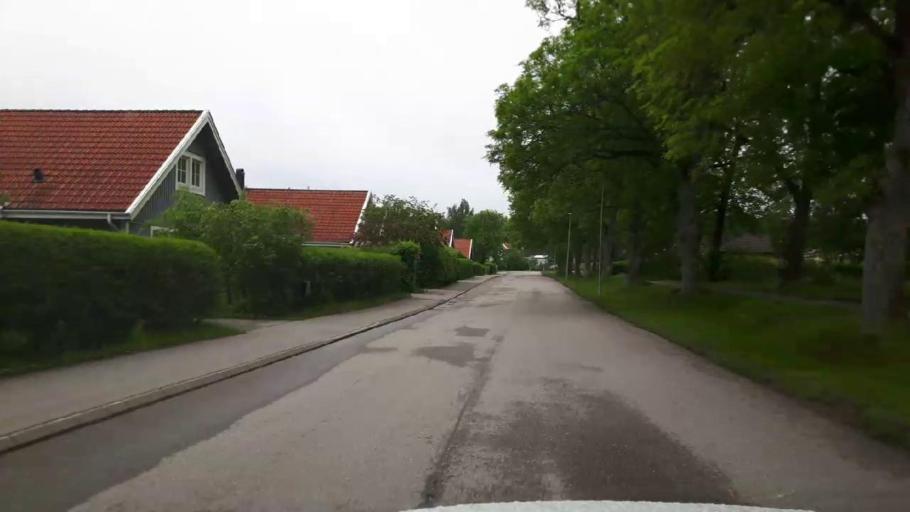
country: SE
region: Stockholm
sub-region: Upplands-Bro Kommun
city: Bro
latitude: 59.5184
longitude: 17.6615
